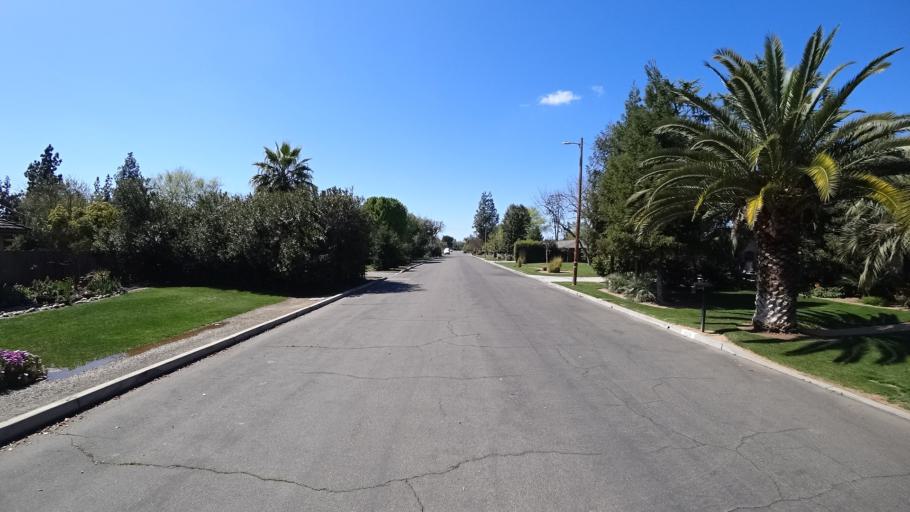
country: US
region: California
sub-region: Fresno County
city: Fresno
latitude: 36.8065
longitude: -119.8223
